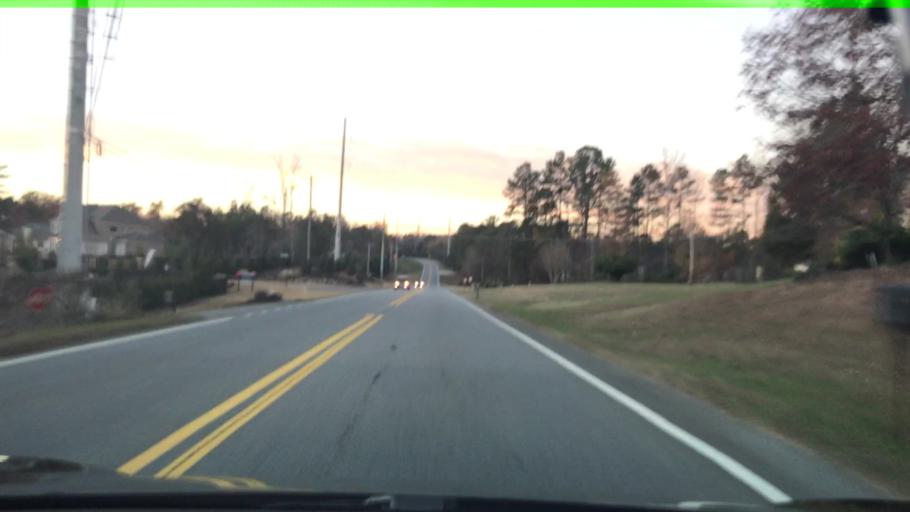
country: US
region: Georgia
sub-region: Gwinnett County
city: Suwanee
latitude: 34.0865
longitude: -84.1319
